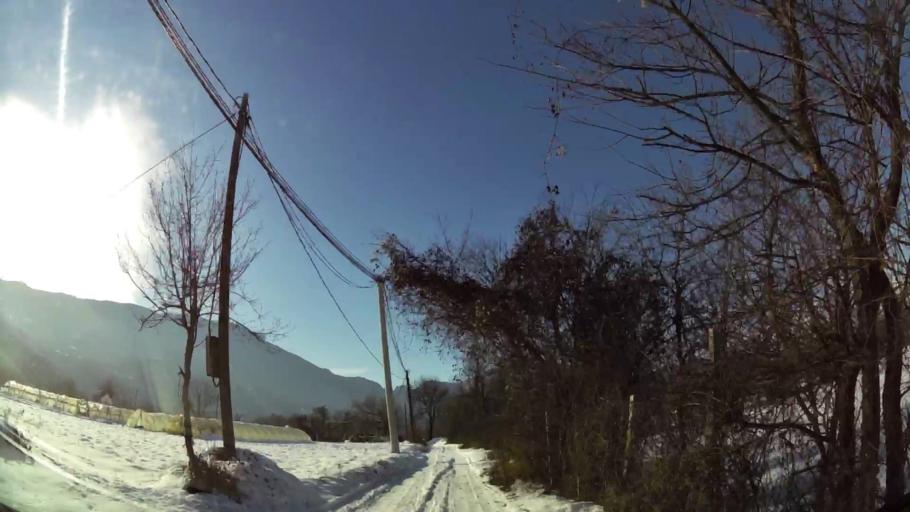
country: MK
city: Grchec
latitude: 41.9867
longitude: 21.3247
